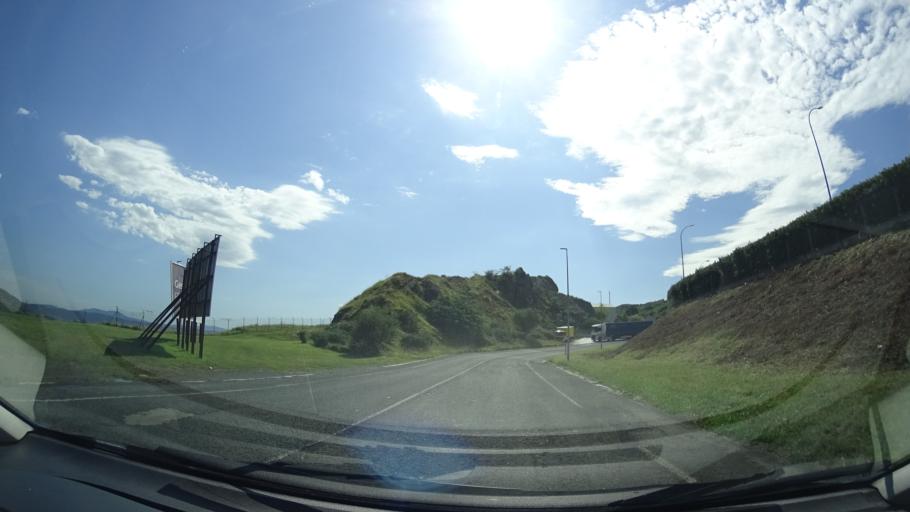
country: ES
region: Basque Country
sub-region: Bizkaia
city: Urtuella
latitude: 43.3082
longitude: -3.0765
